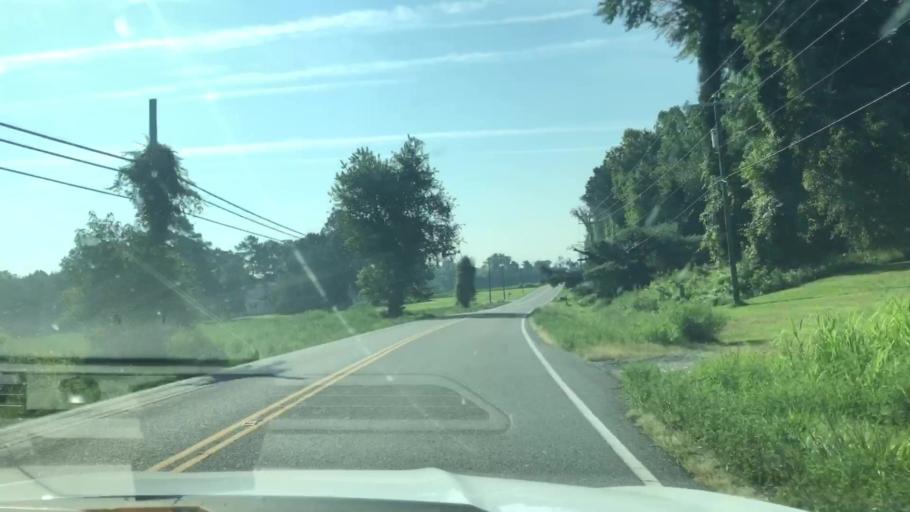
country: US
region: Virginia
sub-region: Richmond County
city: Warsaw
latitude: 37.8972
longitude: -76.6771
